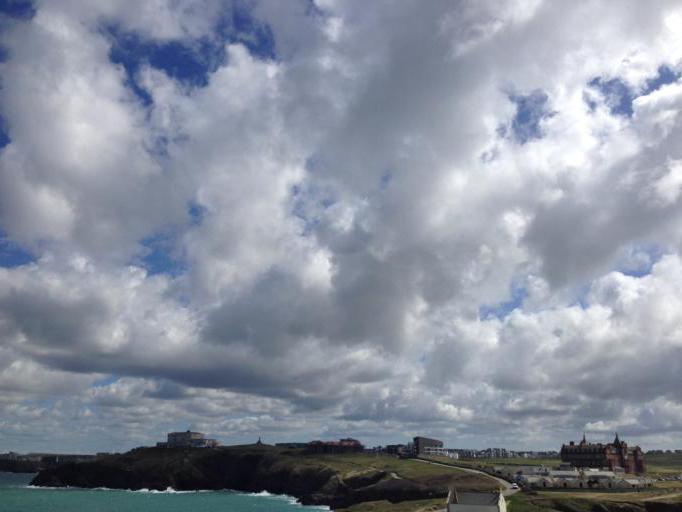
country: GB
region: England
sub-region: Cornwall
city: Newquay
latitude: 50.4246
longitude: -5.0987
